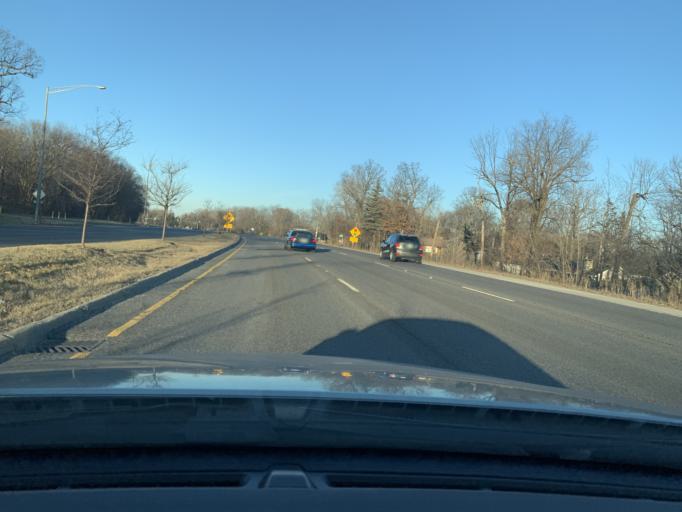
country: US
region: Illinois
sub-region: DuPage County
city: Bensenville
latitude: 41.9424
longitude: -87.9614
